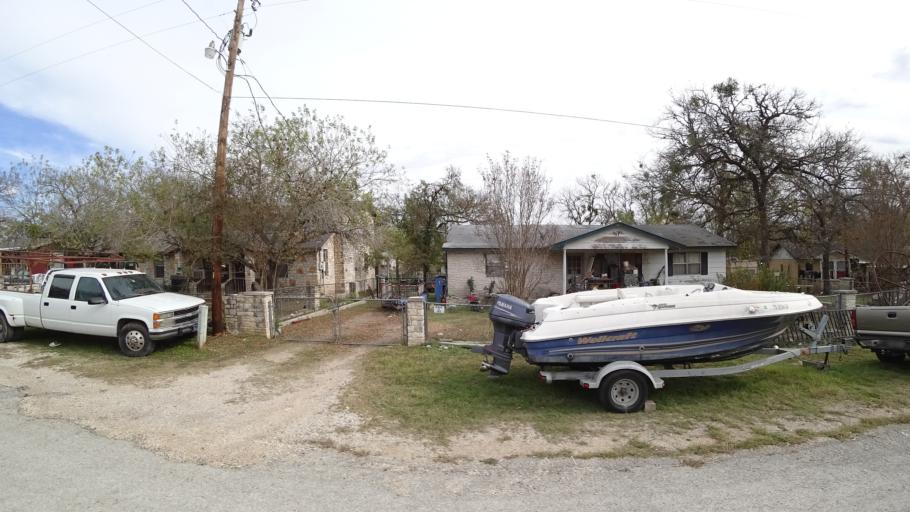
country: US
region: Texas
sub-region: Travis County
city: Garfield
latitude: 30.1360
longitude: -97.5685
